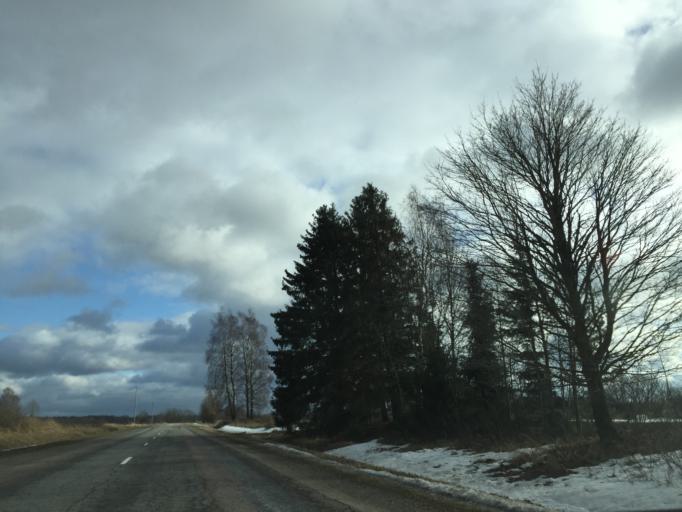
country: LV
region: Aloja
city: Staicele
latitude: 57.8909
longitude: 24.6460
